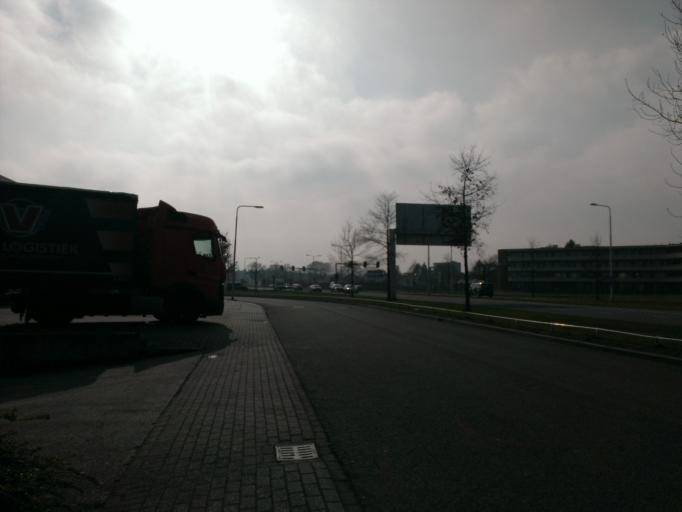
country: NL
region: Overijssel
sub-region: Gemeente Almelo
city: Almelo
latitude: 52.3423
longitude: 6.6824
